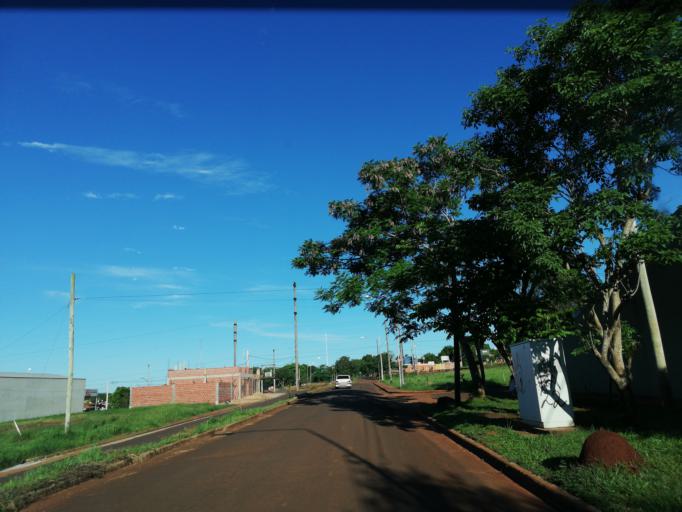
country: AR
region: Misiones
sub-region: Departamento de Capital
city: Posadas
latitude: -27.4358
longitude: -55.9165
